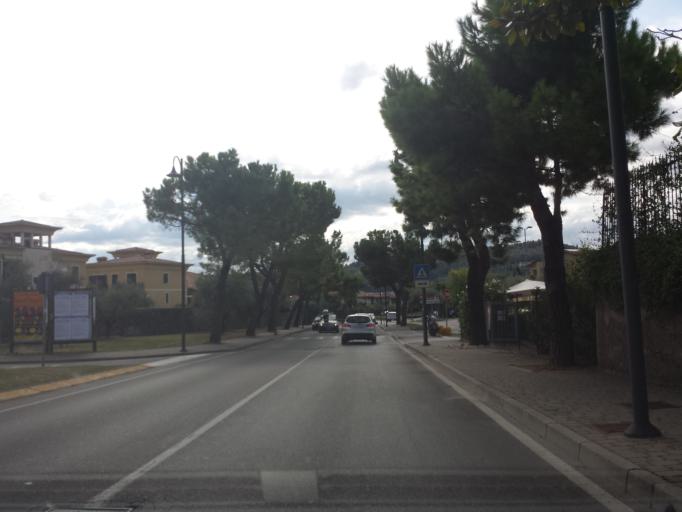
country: IT
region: Lombardy
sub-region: Provincia di Brescia
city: Salo
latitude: 45.6052
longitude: 10.5151
